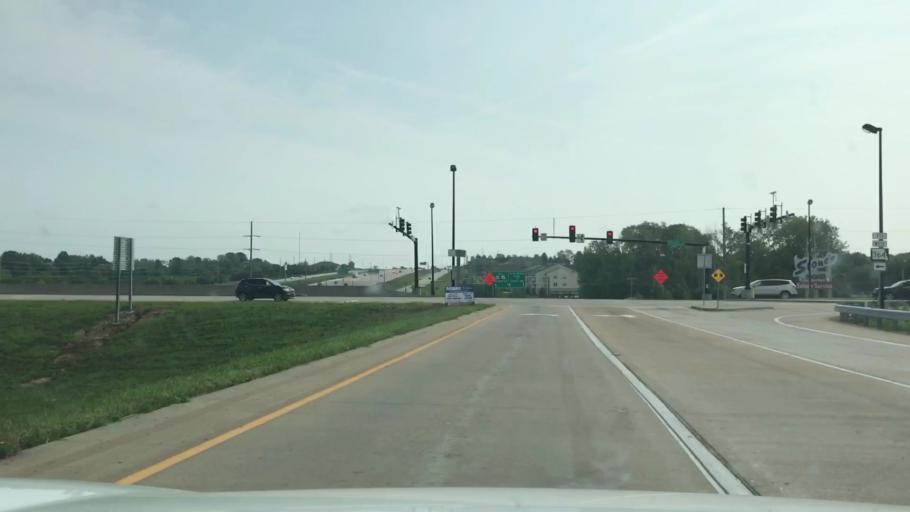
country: US
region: Missouri
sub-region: Saint Charles County
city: Cottleville
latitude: 38.7373
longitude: -90.6345
